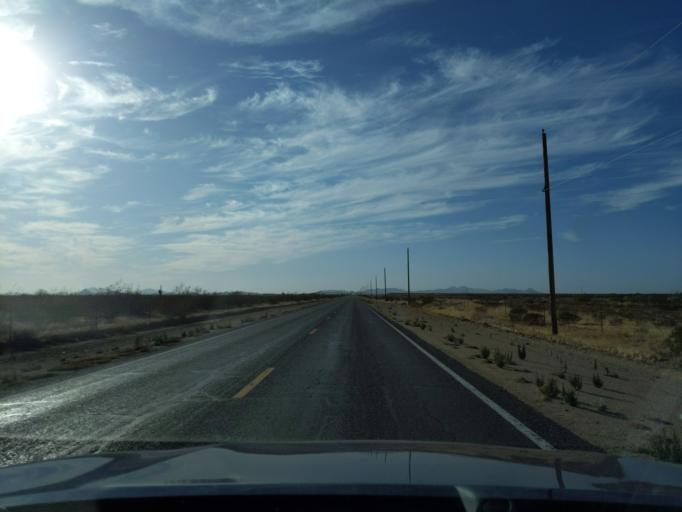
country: US
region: Arizona
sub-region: Pinal County
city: Florence
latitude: 33.1183
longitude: -111.3828
